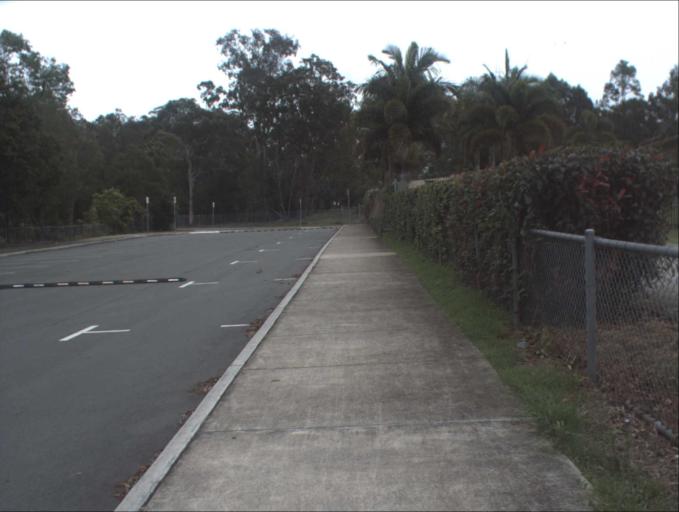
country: AU
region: Queensland
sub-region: Logan
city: Park Ridge South
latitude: -27.6853
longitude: 153.0225
